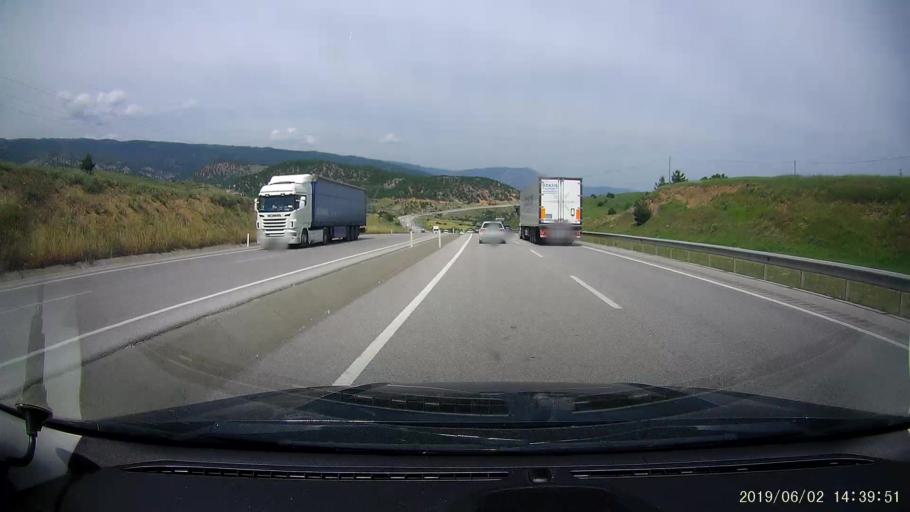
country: TR
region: Corum
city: Hacihamza
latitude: 41.0749
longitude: 34.3090
